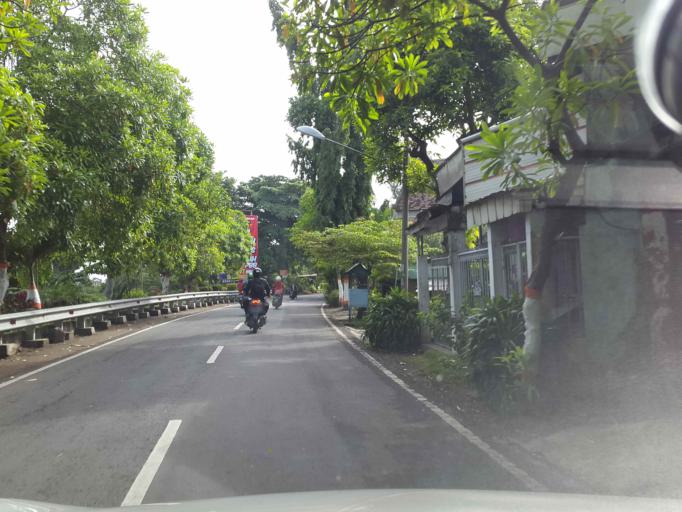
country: ID
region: East Java
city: Mojokerto
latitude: -7.4620
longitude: 112.4290
